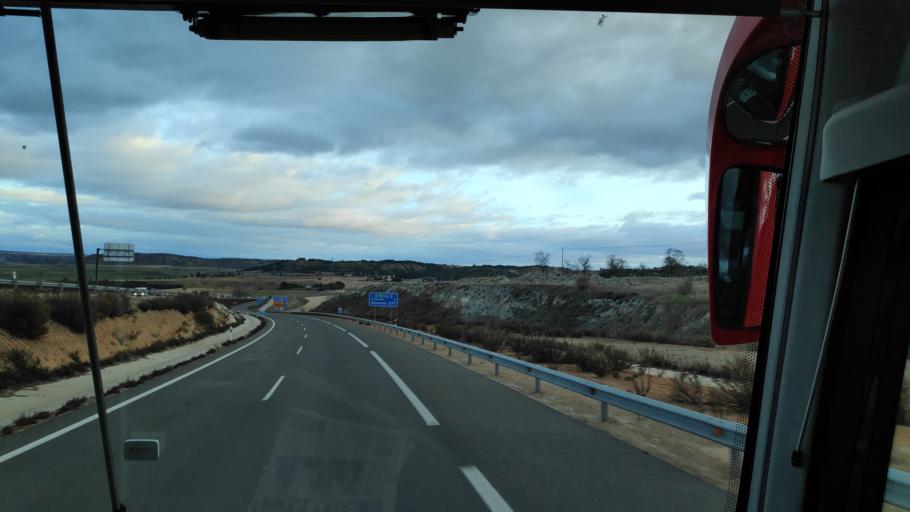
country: ES
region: Castille-La Mancha
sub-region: Provincia de Cuenca
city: Belinchon
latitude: 40.0440
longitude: -3.0601
